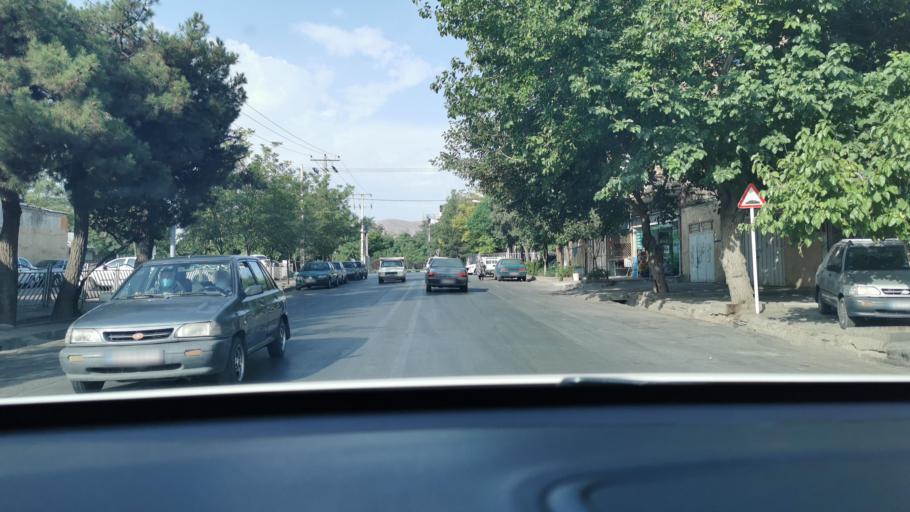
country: IR
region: Razavi Khorasan
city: Mashhad
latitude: 36.2577
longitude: 59.6111
